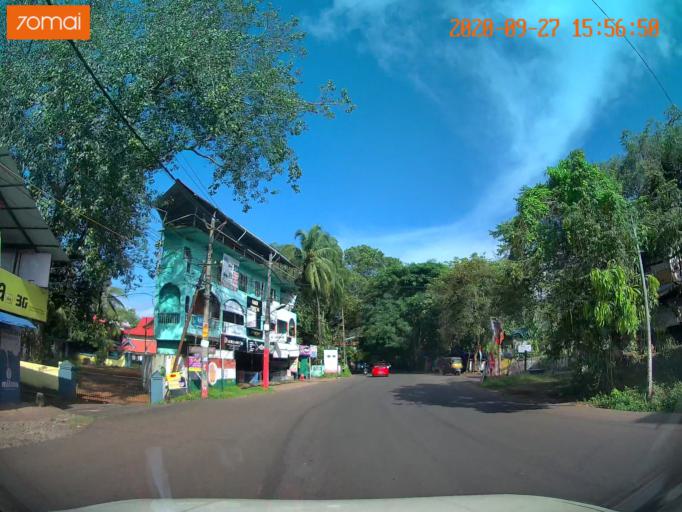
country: IN
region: Kerala
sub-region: Thrissur District
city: Trichur
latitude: 10.5179
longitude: 76.1822
